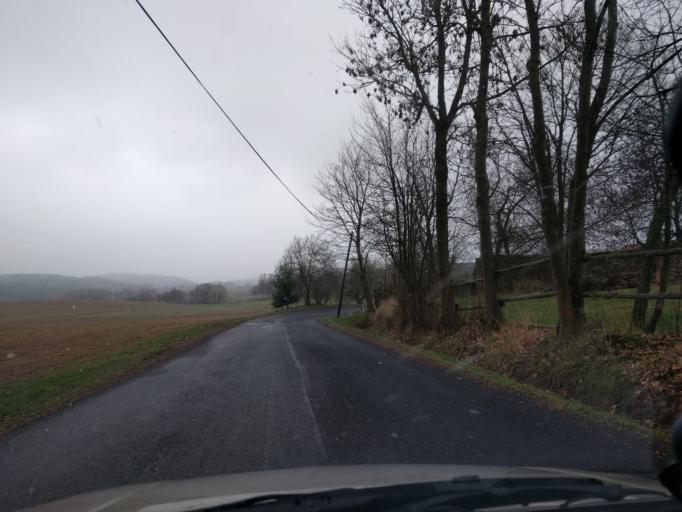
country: CZ
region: Karlovarsky
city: Bochov
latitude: 50.1370
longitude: 13.0884
